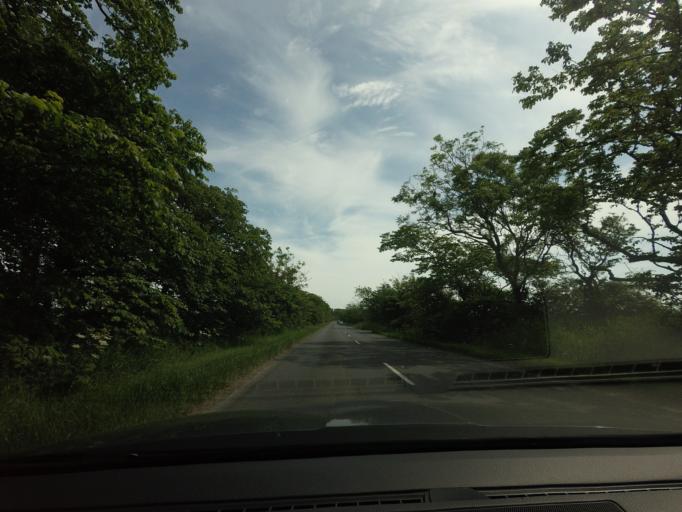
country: GB
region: Scotland
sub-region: Aberdeenshire
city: Peterhead
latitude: 57.5073
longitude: -1.8335
